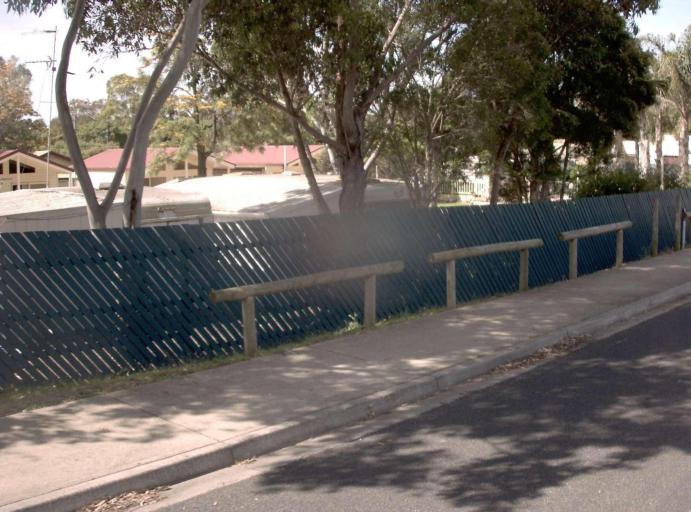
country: AU
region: Victoria
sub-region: East Gippsland
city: Bairnsdale
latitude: -37.8169
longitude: 147.7376
